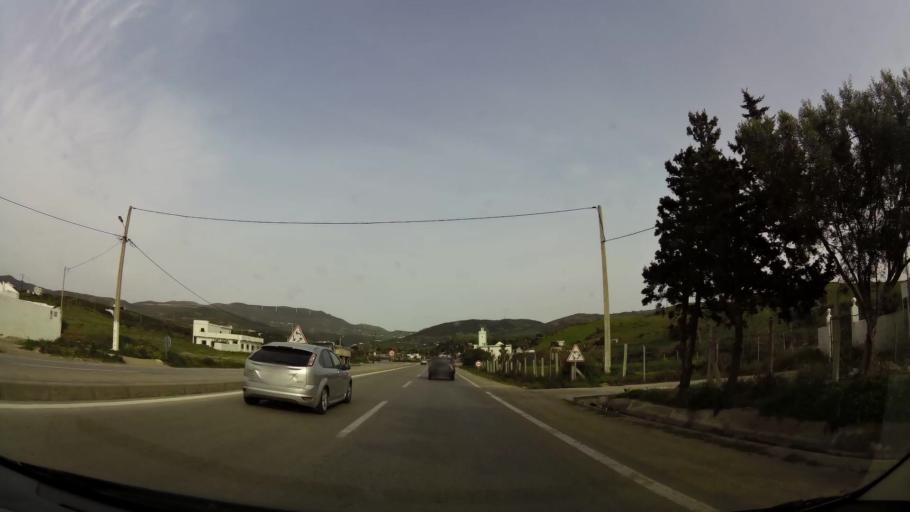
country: MA
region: Tanger-Tetouan
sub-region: Tanger-Assilah
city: Dar Chaoui
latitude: 35.5686
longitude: -5.6185
